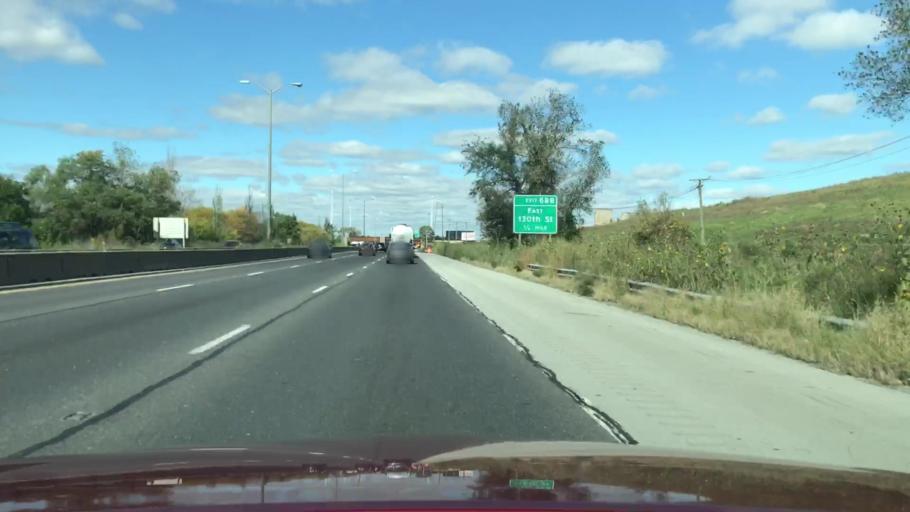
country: US
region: Illinois
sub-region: Cook County
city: Dolton
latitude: 41.6546
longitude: -87.5840
